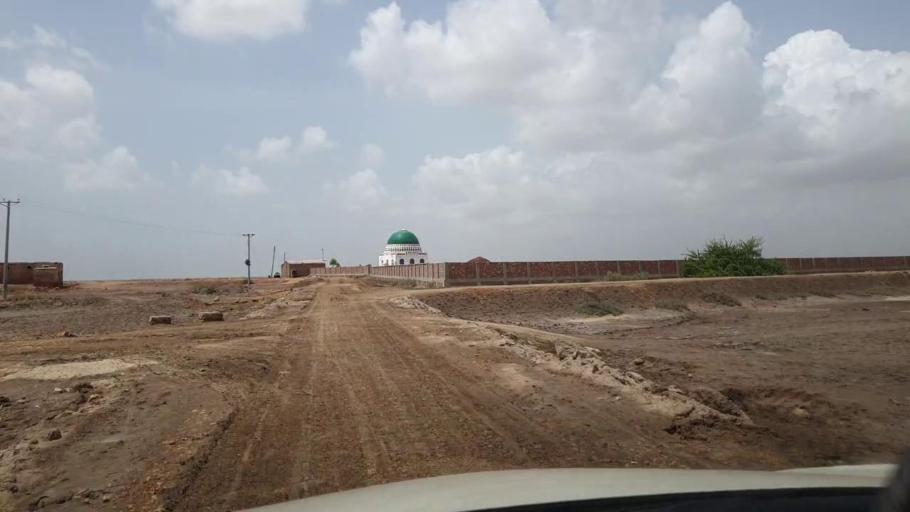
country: PK
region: Sindh
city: Kadhan
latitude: 24.3609
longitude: 68.8468
